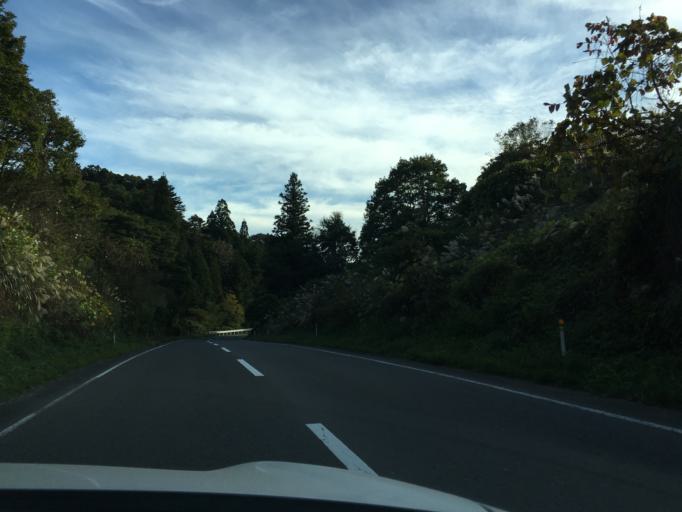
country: JP
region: Fukushima
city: Ishikawa
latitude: 37.2061
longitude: 140.5480
